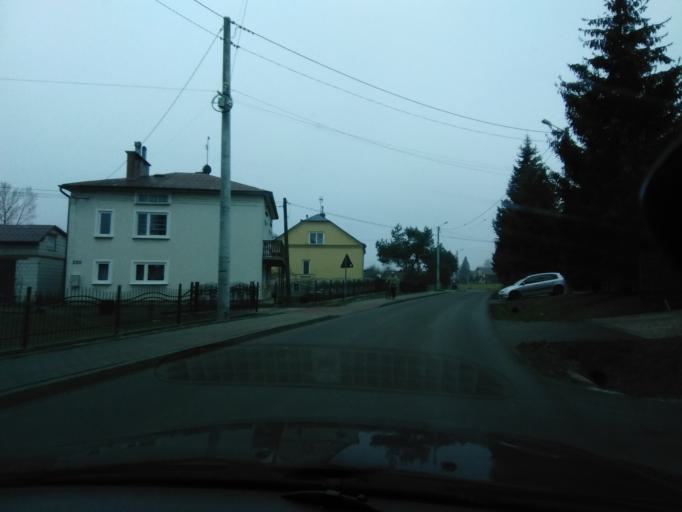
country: PL
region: Subcarpathian Voivodeship
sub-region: Powiat lancucki
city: Sonina
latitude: 50.0534
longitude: 22.2637
